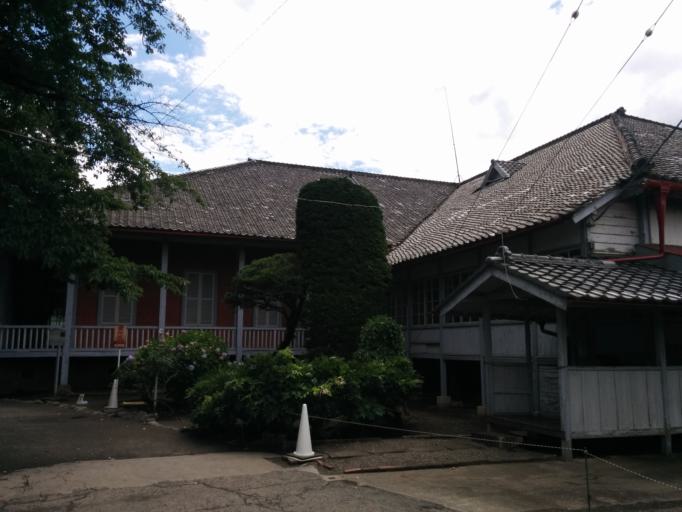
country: JP
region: Gunma
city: Tomioka
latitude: 36.2548
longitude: 138.8883
